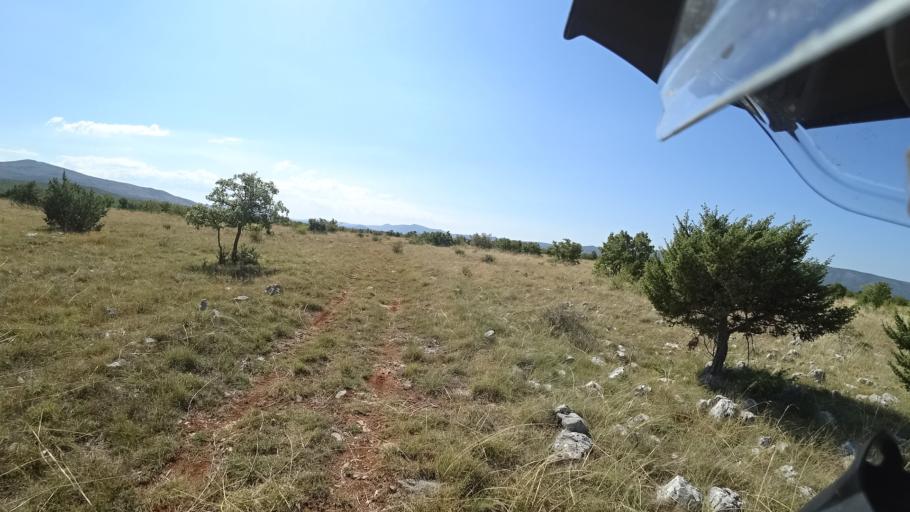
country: HR
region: Sibensko-Kniniska
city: Drnis
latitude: 43.8587
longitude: 16.2735
